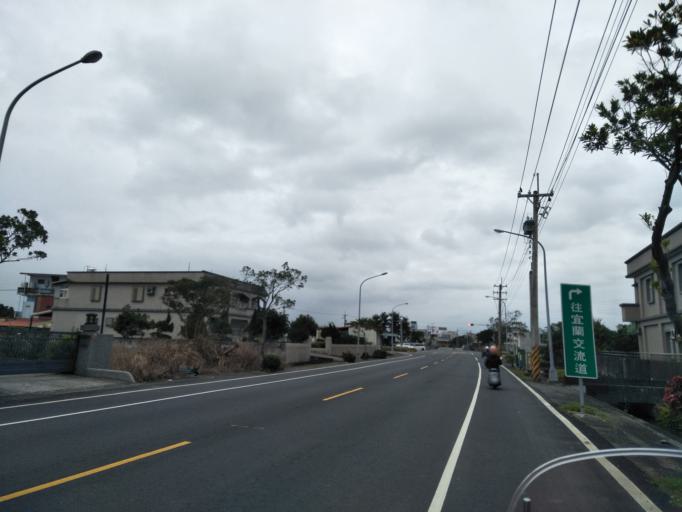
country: TW
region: Taiwan
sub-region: Yilan
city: Yilan
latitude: 24.7766
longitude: 121.7830
